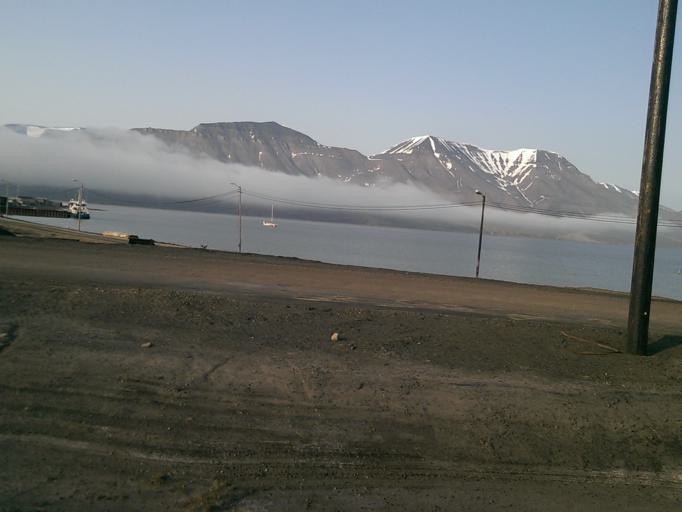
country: SJ
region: Svalbard
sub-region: Spitsbergen
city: Longyearbyen
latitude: 78.2406
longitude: 15.5323
